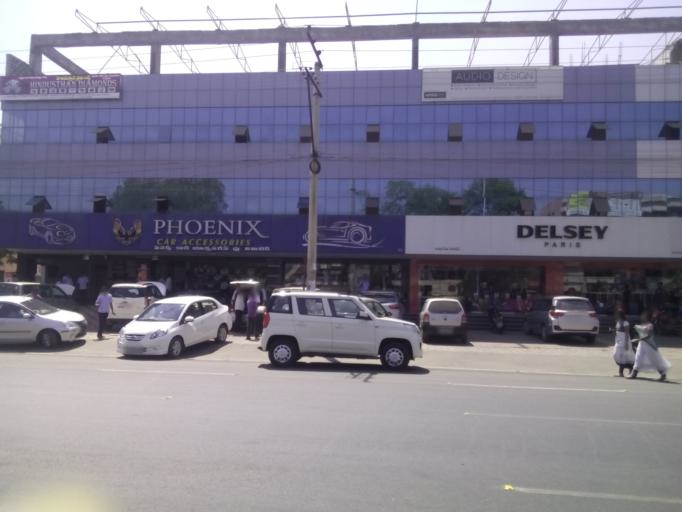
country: IN
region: Andhra Pradesh
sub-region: Krishna
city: Vijayawada
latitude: 16.5046
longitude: 80.6363
